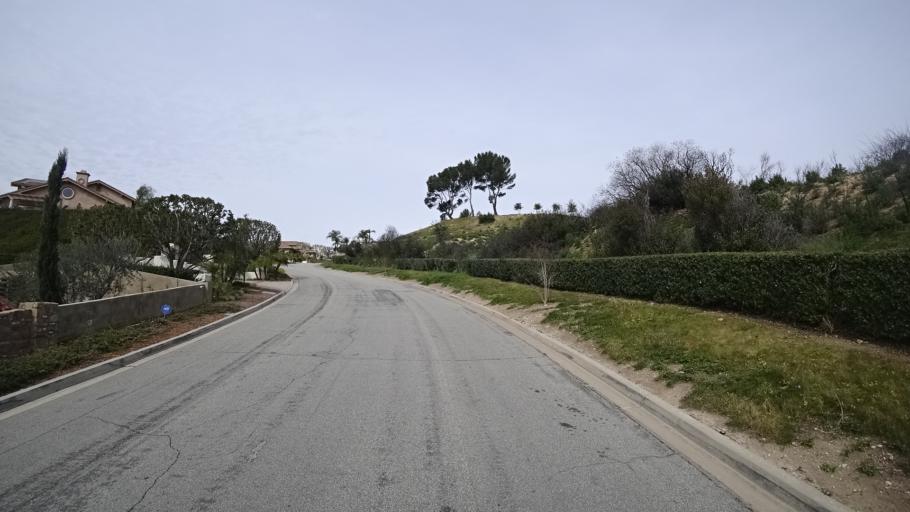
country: US
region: California
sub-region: Orange County
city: Villa Park
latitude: 33.8341
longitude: -117.7431
